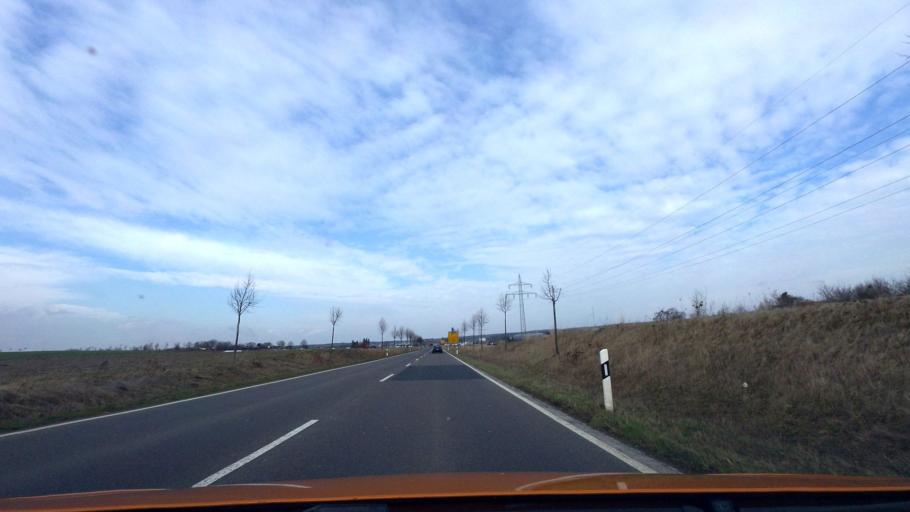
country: DE
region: Lower Saxony
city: Helmstedt
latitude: 52.2253
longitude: 10.9916
